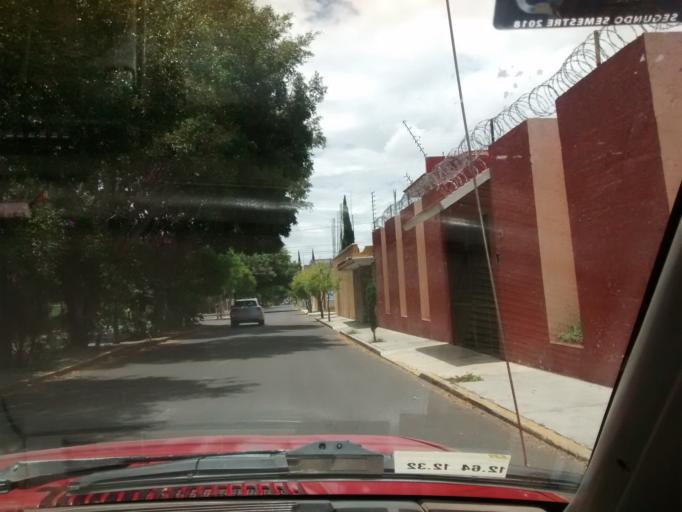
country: MX
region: Puebla
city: Tehuacan
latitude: 18.4624
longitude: -97.4083
